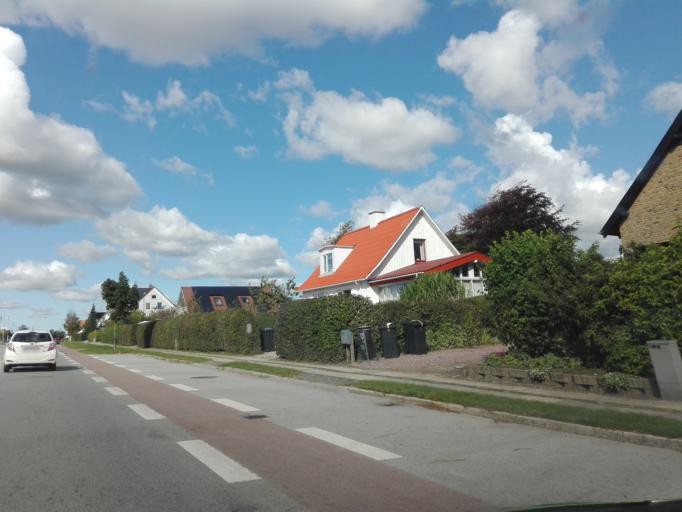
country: DK
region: North Denmark
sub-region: Mariagerfjord Kommune
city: Hobro
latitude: 56.6292
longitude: 9.8023
